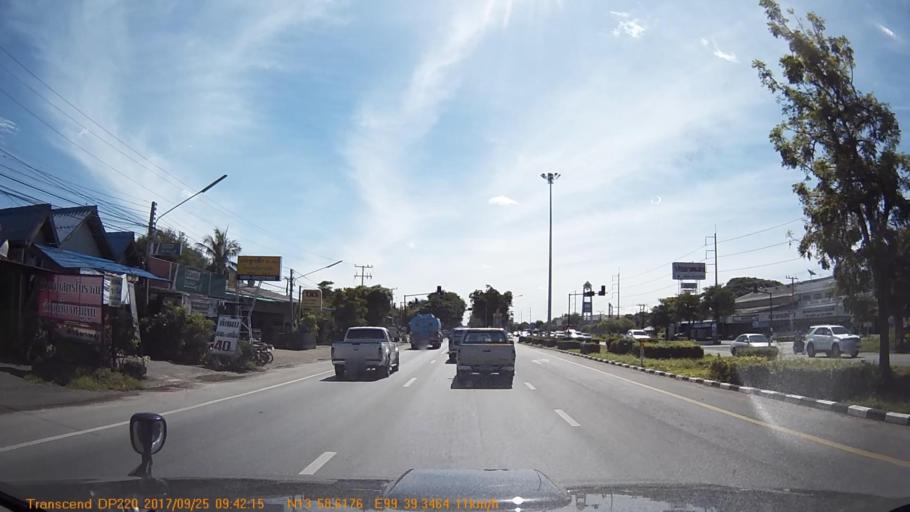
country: TH
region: Kanchanaburi
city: Tha Muang
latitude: 13.9770
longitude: 99.6558
